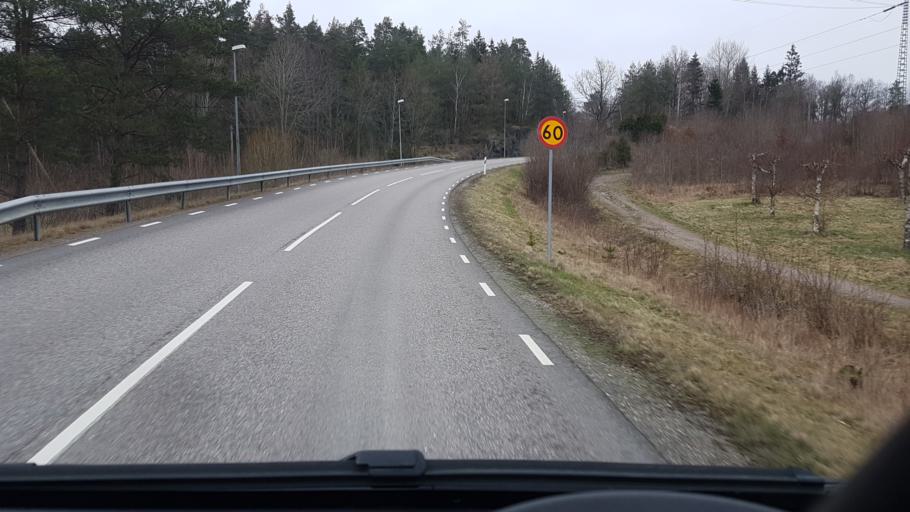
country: SE
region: Vaestra Goetaland
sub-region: Lerums Kommun
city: Stenkullen
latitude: 57.8050
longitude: 12.3333
